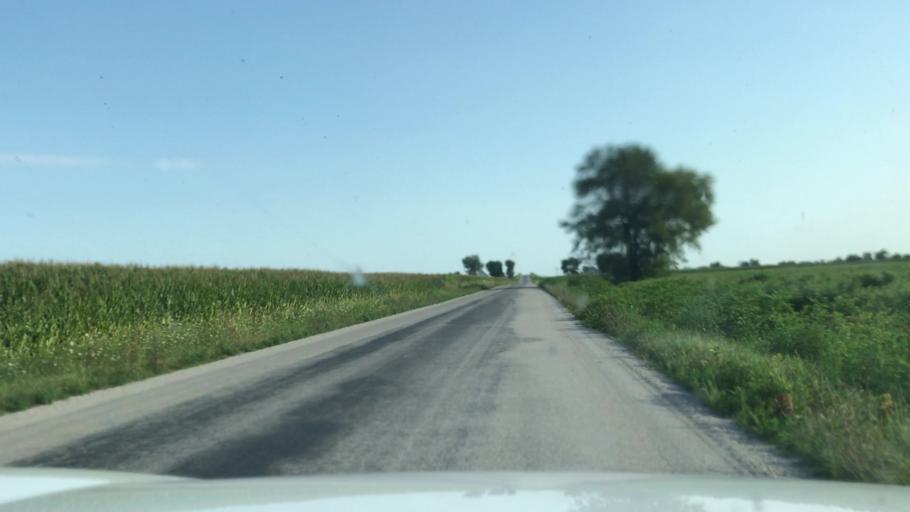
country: US
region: Illinois
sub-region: Washington County
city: Okawville
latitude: 38.4355
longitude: -89.4779
